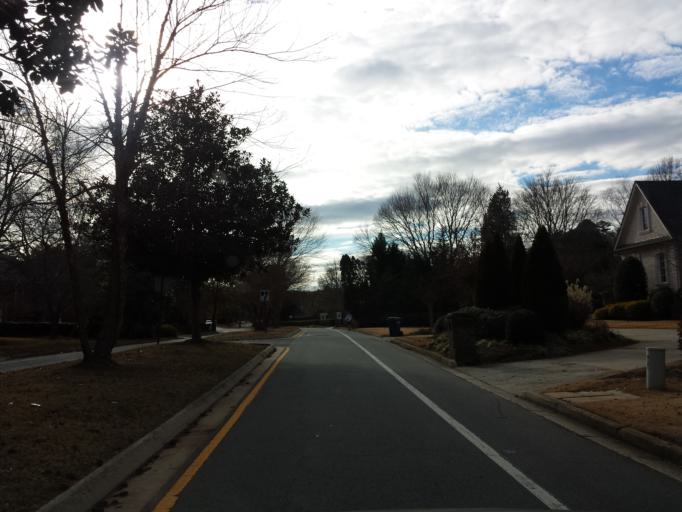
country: US
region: Georgia
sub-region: Fulton County
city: Sandy Springs
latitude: 33.9294
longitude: -84.4253
